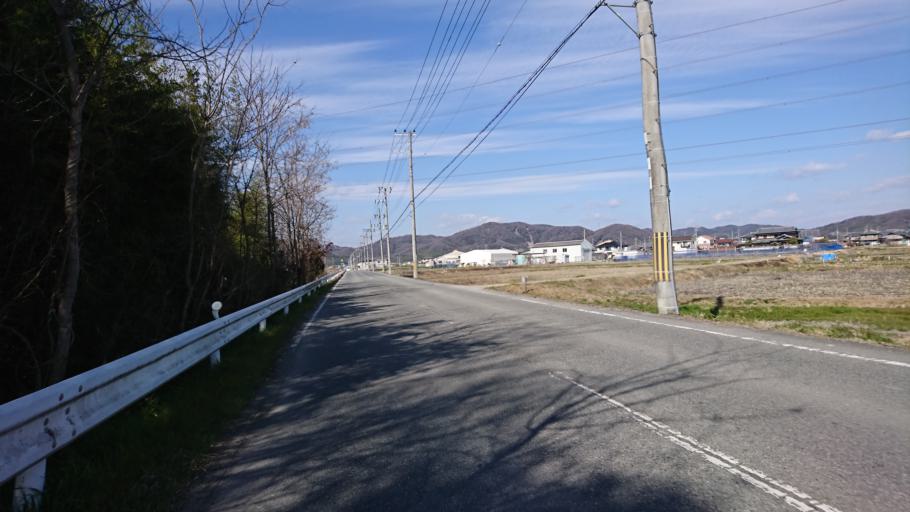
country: JP
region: Hyogo
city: Kakogawacho-honmachi
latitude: 34.8042
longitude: 134.8114
